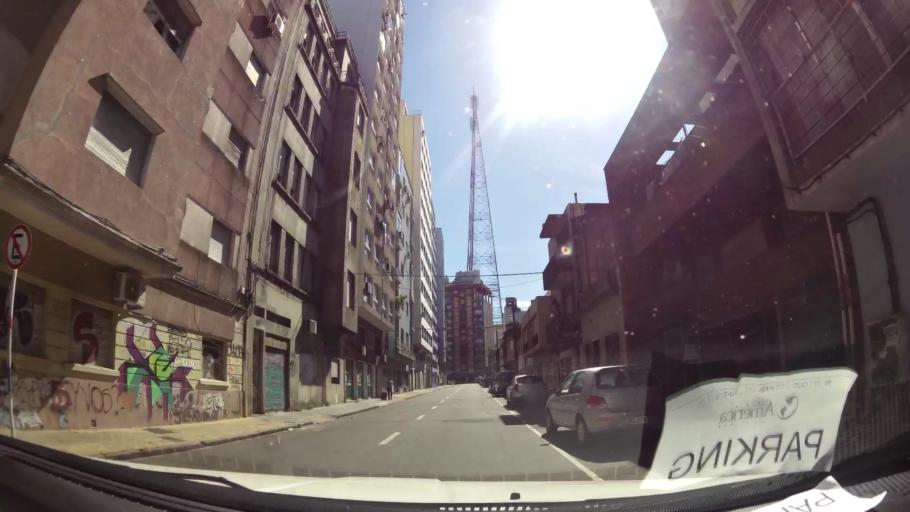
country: UY
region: Montevideo
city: Montevideo
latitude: -34.8993
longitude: -56.1685
